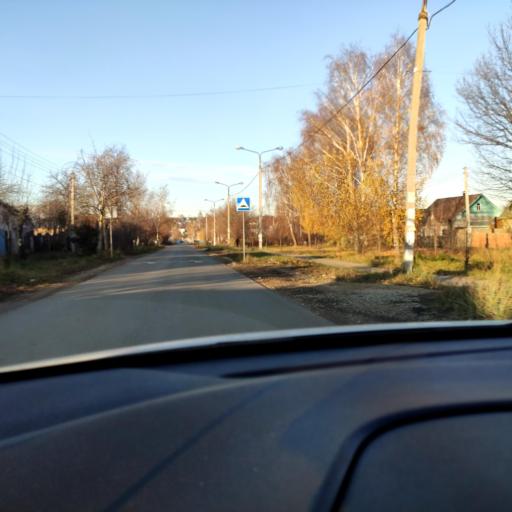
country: RU
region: Tatarstan
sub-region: Gorod Kazan'
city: Kazan
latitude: 55.8785
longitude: 49.0698
